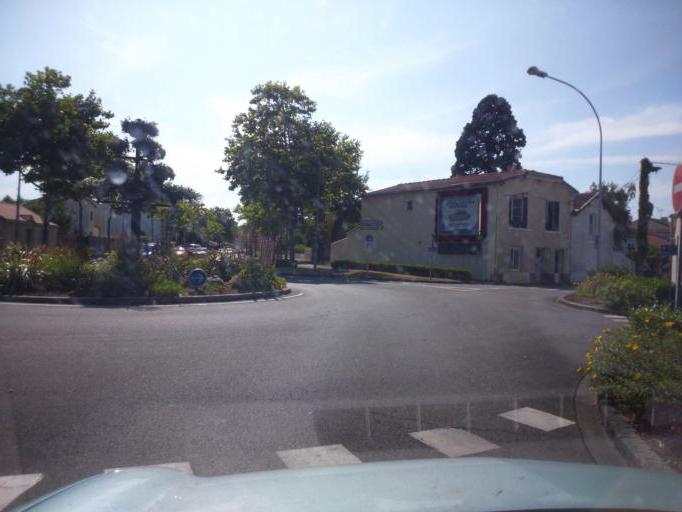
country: FR
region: Pays de la Loire
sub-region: Departement de la Loire-Atlantique
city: Saint-Sebastien-sur-Loire
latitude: 47.1995
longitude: -1.5206
